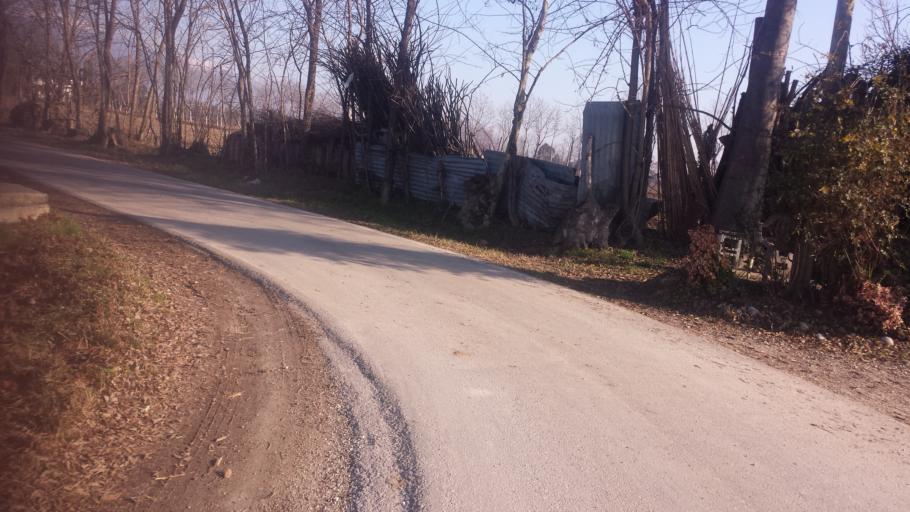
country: IT
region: Veneto
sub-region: Provincia di Vicenza
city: Rosa
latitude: 45.7129
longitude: 11.7544
